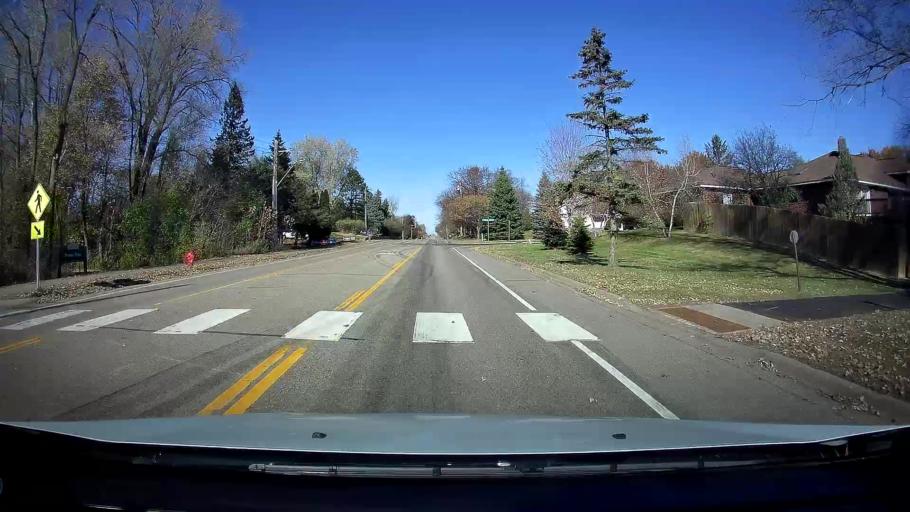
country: US
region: Minnesota
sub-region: Ramsey County
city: Shoreview
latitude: 45.0683
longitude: -93.1574
